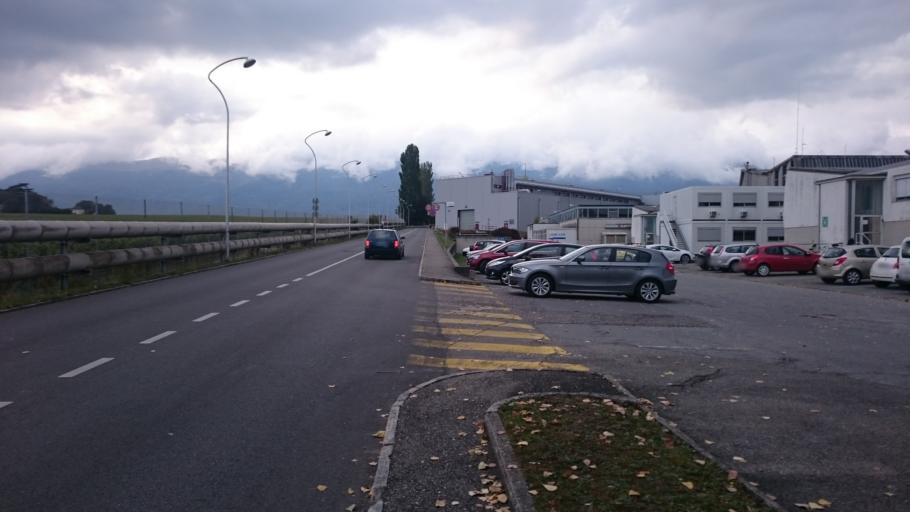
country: CH
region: Geneva
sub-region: Geneva
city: Satigny
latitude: 46.2299
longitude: 6.0486
